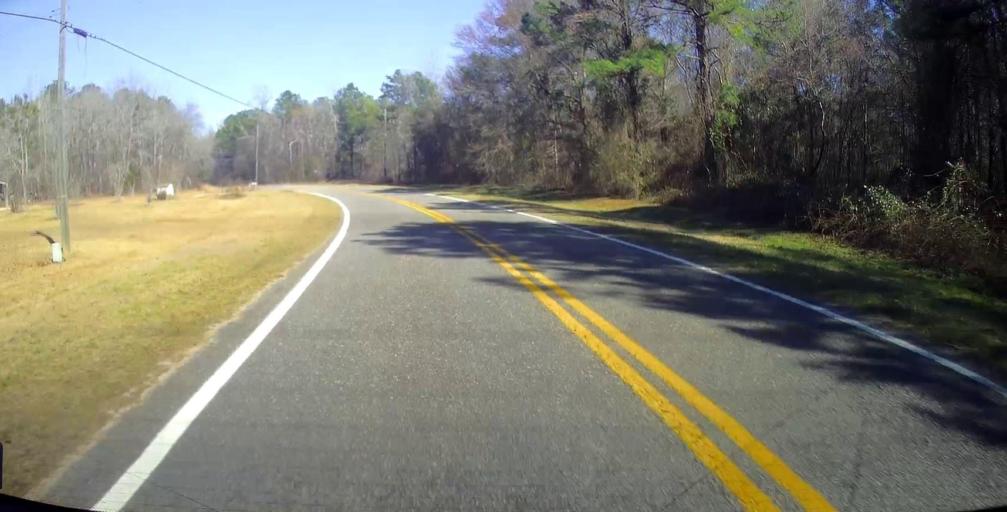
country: US
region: Georgia
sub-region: Peach County
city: Fort Valley
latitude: 32.6401
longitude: -83.9207
